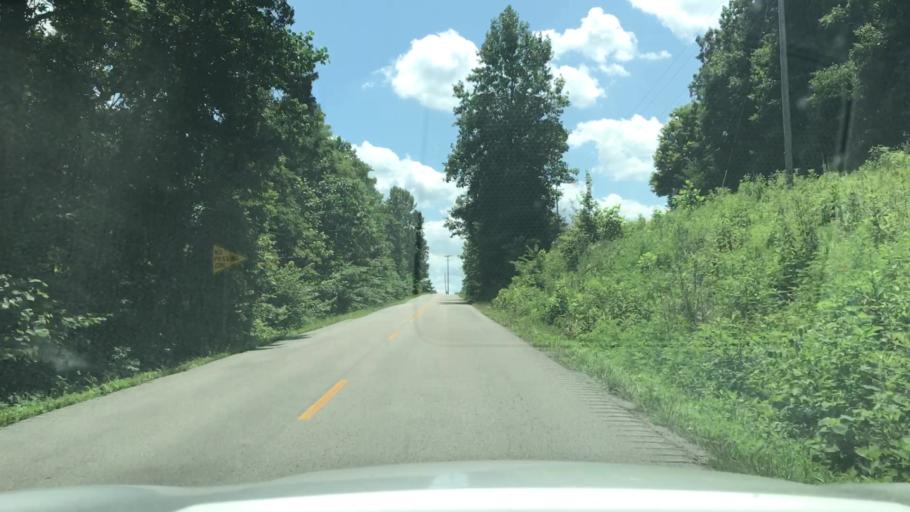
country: US
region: Kentucky
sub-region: Hopkins County
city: Nortonville
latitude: 37.0394
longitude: -87.3500
